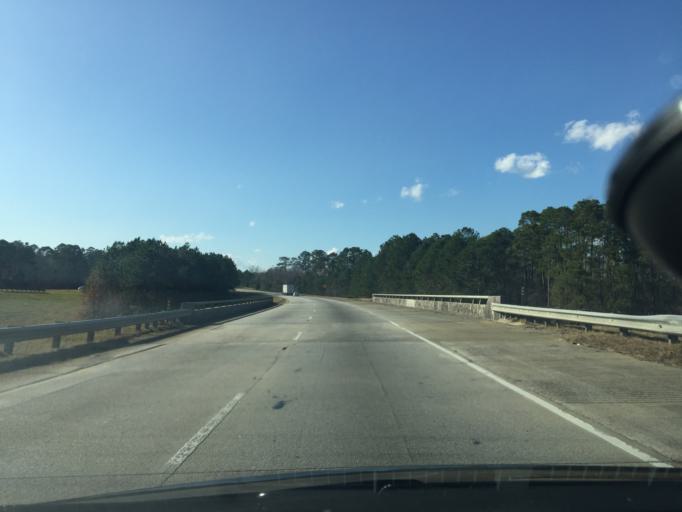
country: US
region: Georgia
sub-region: Treutlen County
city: Soperton
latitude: 32.4352
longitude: -82.4999
